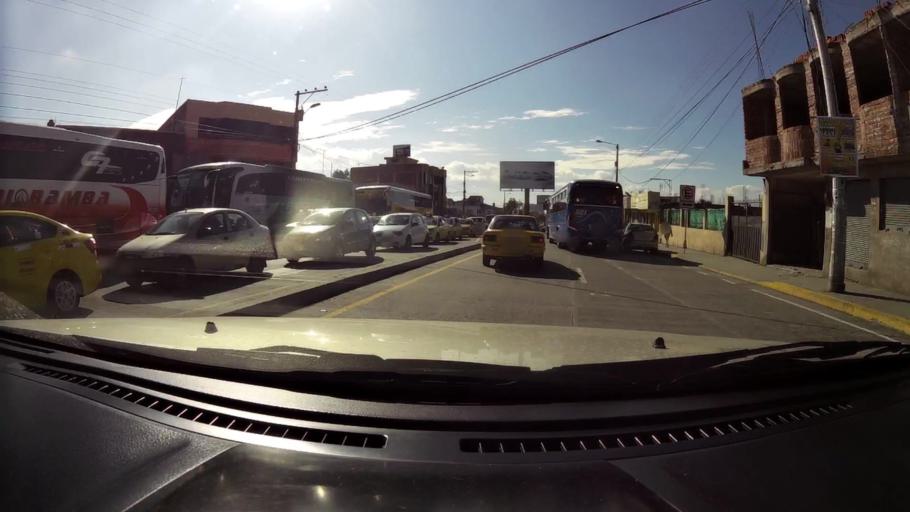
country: EC
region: Chimborazo
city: Riobamba
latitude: -1.6451
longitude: -78.6736
